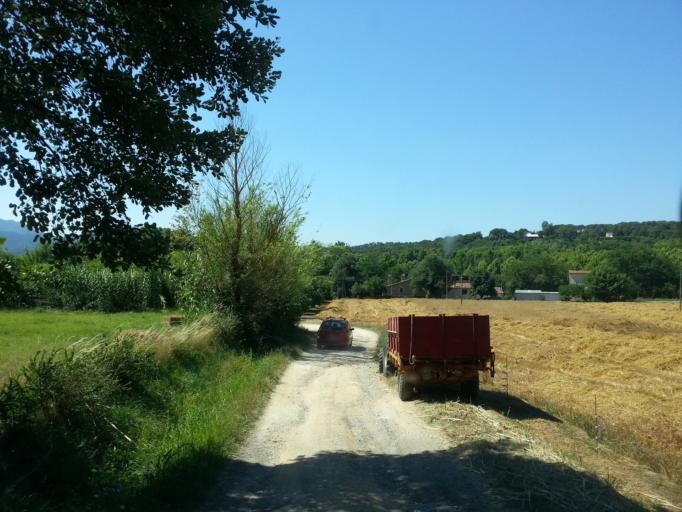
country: ES
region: Catalonia
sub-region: Provincia de Girona
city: Breda
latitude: 41.7260
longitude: 2.5174
